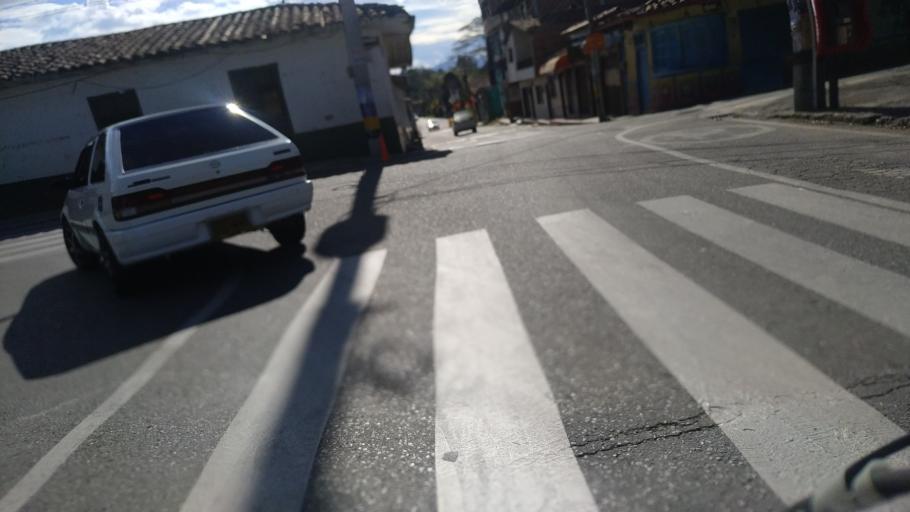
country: CO
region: Antioquia
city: Rionegro
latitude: 6.1304
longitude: -75.3803
